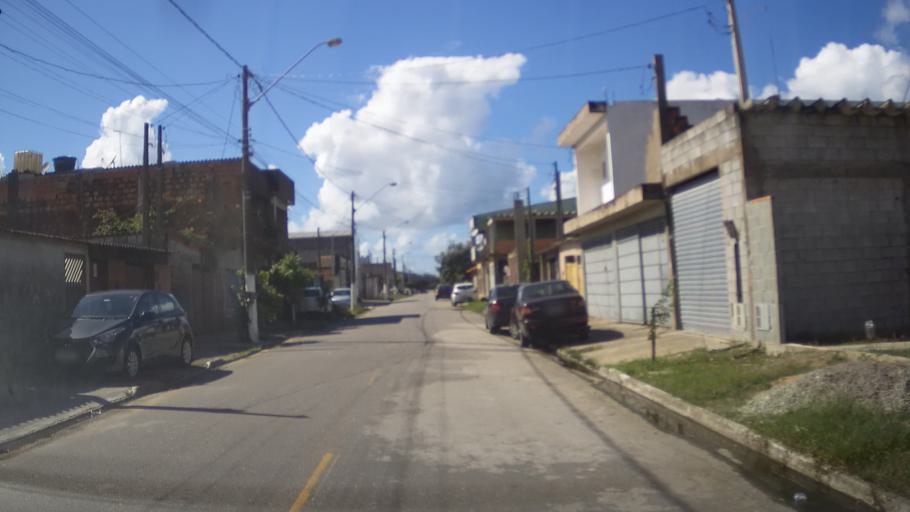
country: BR
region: Sao Paulo
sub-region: Praia Grande
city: Praia Grande
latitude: -24.0213
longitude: -46.5087
